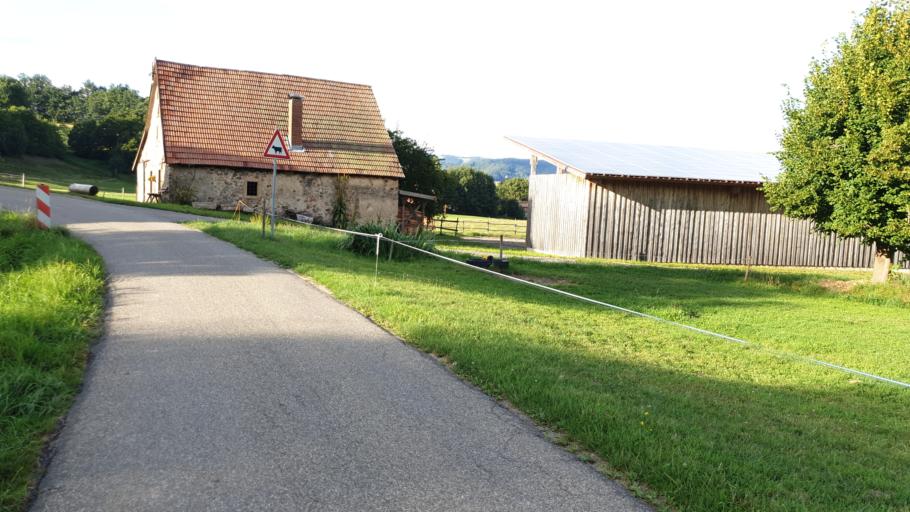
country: DE
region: Baden-Wuerttemberg
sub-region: Freiburg Region
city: Kirchzarten
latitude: 47.9534
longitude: 7.9462
